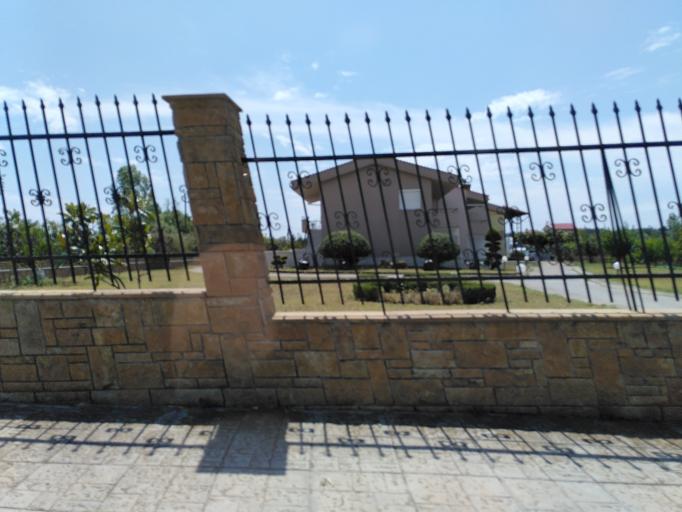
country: GR
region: Central Macedonia
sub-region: Nomos Thessalonikis
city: Agia Triada
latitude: 40.4926
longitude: 22.8664
